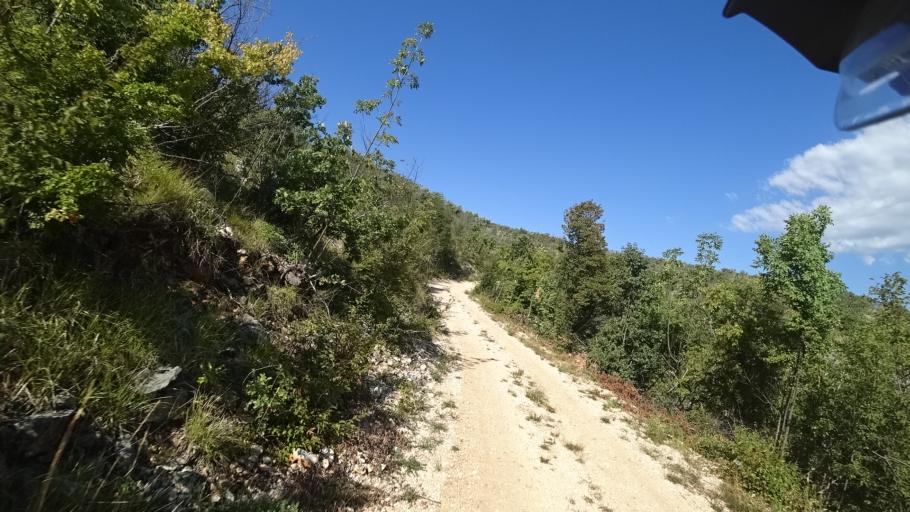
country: HR
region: Sibensko-Kniniska
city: Knin
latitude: 43.9590
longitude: 16.1596
